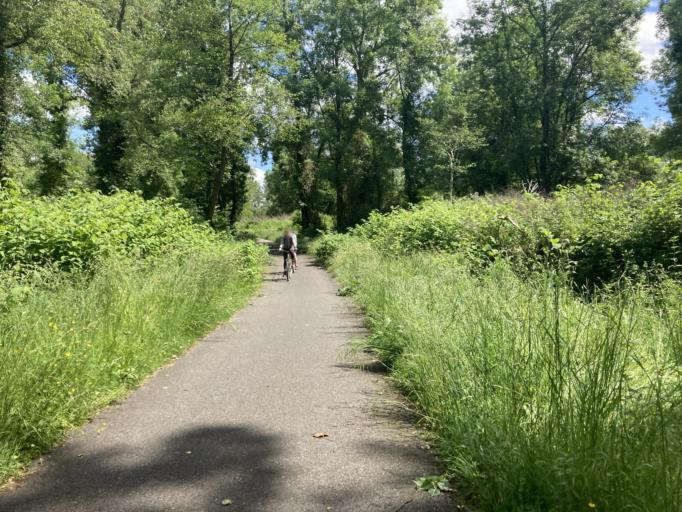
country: FR
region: Aquitaine
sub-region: Departement des Pyrenees-Atlantiques
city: Artiguelouve
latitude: 43.3296
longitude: -0.4680
